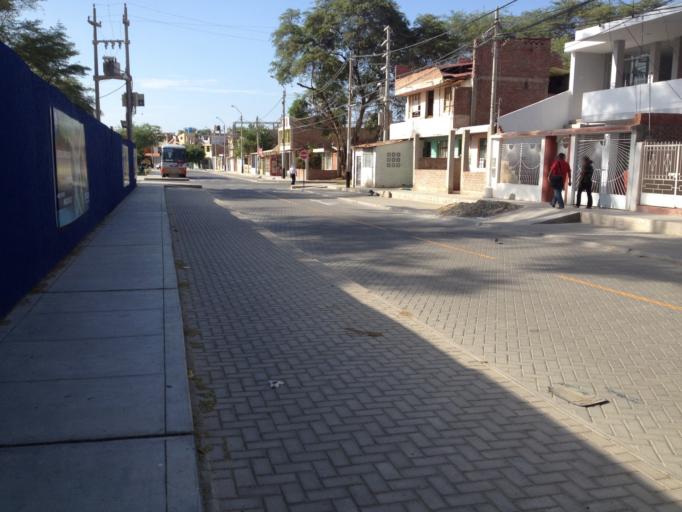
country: PE
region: Piura
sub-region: Provincia de Piura
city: Piura
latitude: -5.1867
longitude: -80.6477
